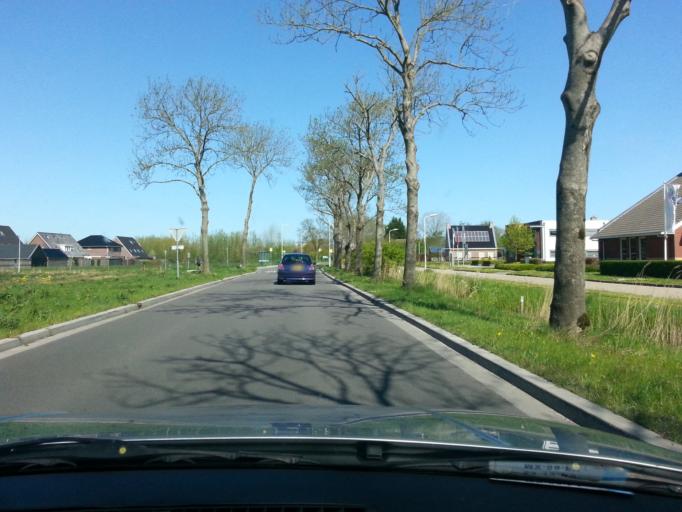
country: NL
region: Friesland
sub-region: Gemeente Achtkarspelen
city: Buitenpost
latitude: 53.2433
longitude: 6.1556
